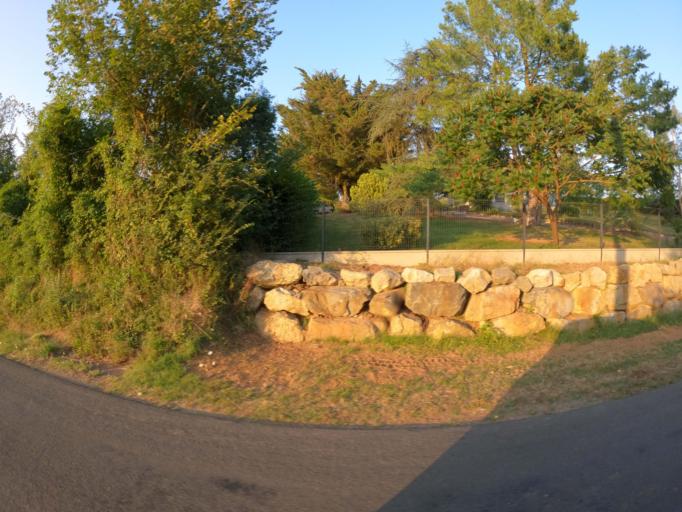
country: FR
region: Pays de la Loire
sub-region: Departement de la Sarthe
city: Parce-sur-Sarthe
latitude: 47.8604
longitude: -0.1976
